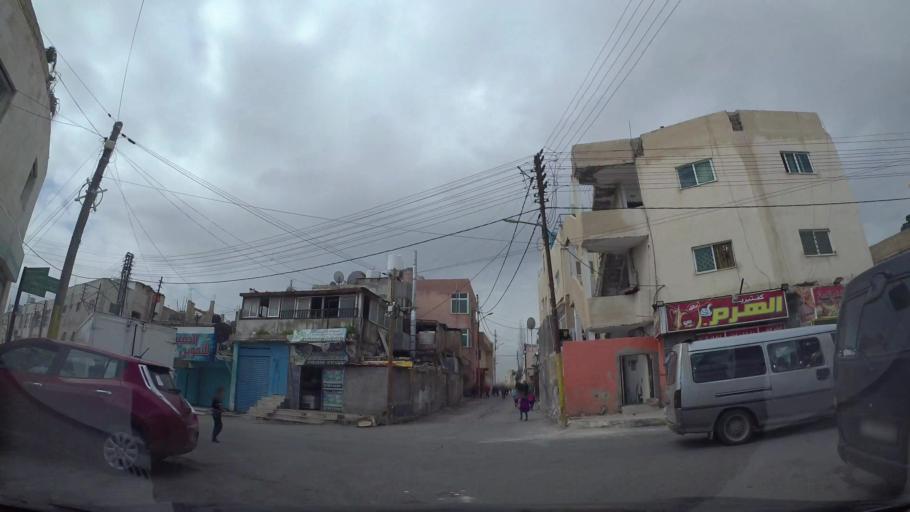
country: JO
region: Amman
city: Amman
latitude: 31.9831
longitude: 35.9213
